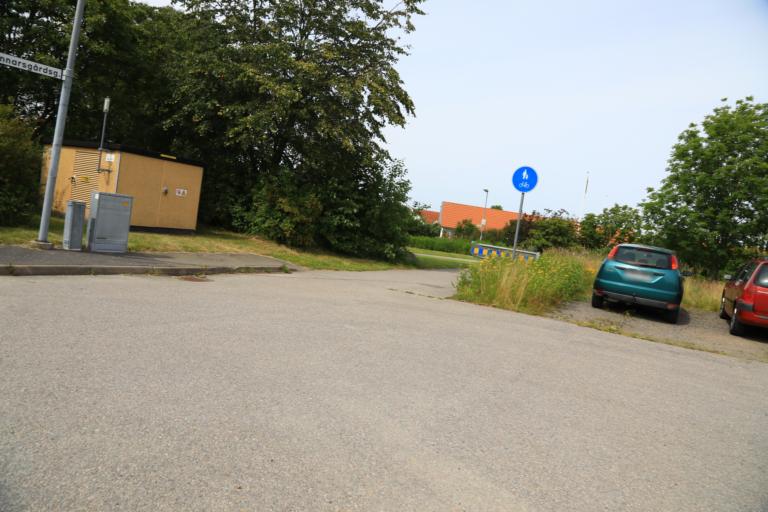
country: SE
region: Halland
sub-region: Varbergs Kommun
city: Traslovslage
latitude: 57.1088
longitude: 12.2970
